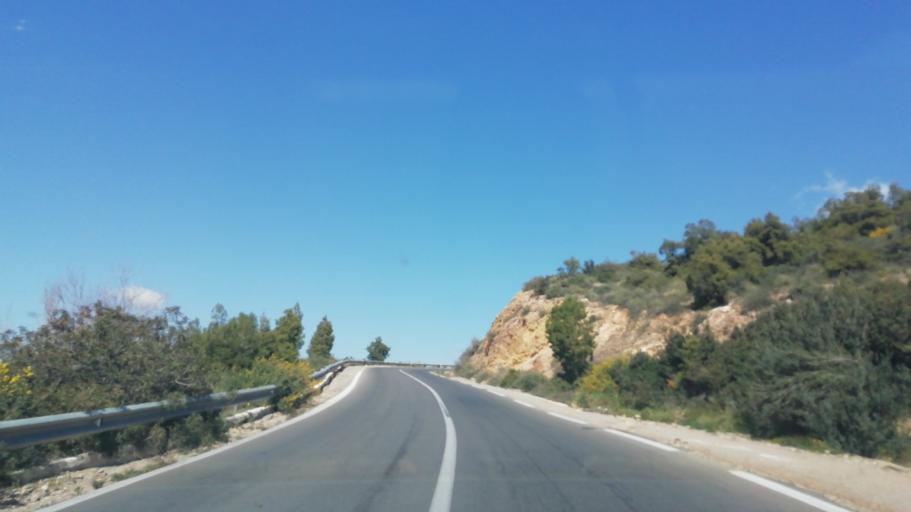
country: DZ
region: Mascara
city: Mascara
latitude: 35.4881
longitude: 0.1471
